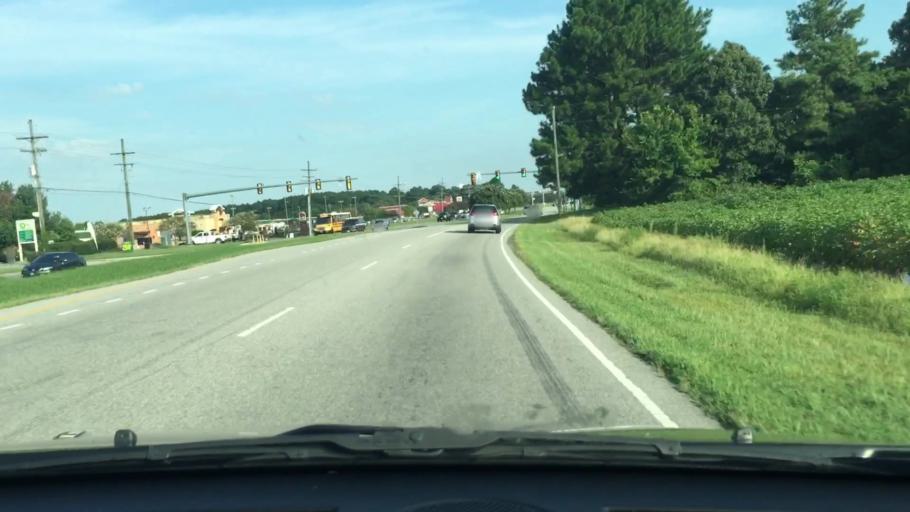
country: US
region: Virginia
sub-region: Isle of Wight County
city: Carrollton
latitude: 36.9538
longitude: -76.6003
